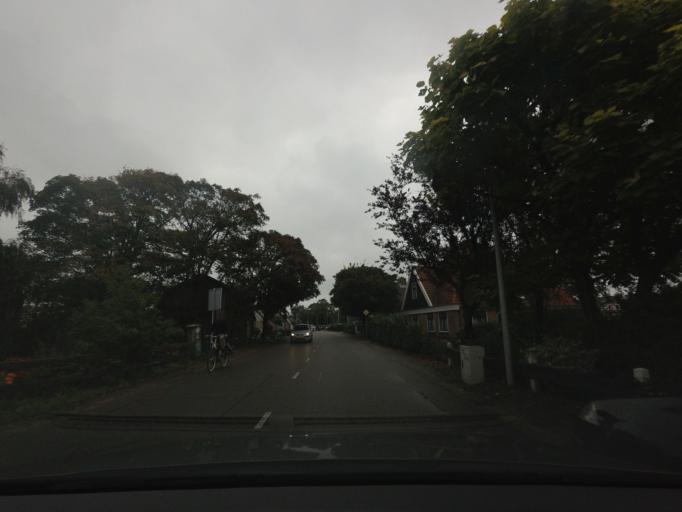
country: NL
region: North Holland
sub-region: Gemeente Alkmaar
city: Alkmaar
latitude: 52.6490
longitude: 4.7779
